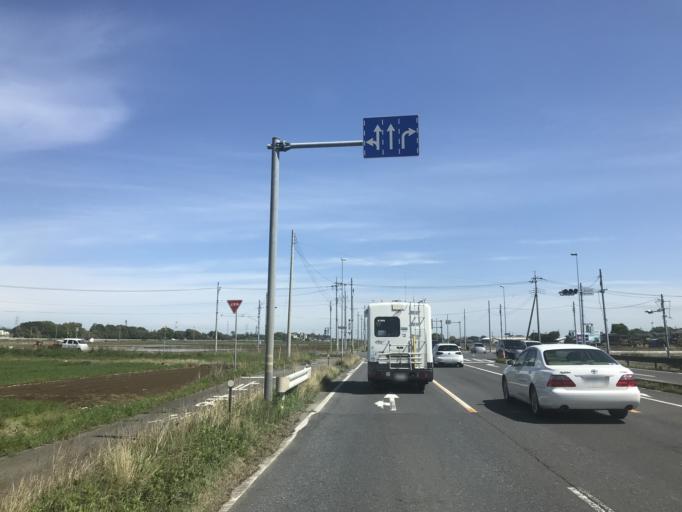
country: JP
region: Ibaraki
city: Ishige
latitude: 36.2047
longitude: 139.9844
